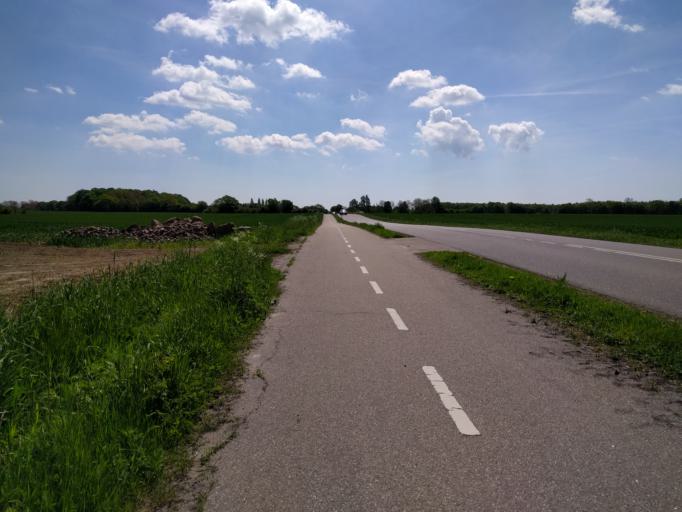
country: DK
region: Zealand
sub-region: Guldborgsund Kommune
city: Nykobing Falster
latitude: 54.7548
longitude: 11.9303
